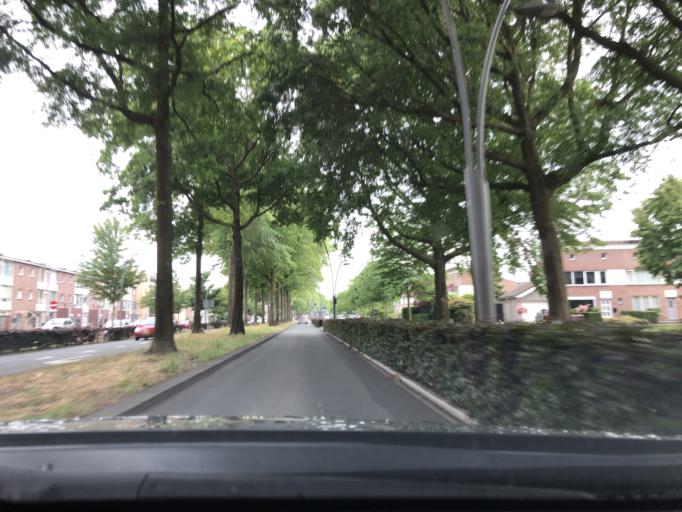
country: NL
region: North Brabant
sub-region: Gemeente Oss
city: Berghem
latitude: 51.7733
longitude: 5.5445
